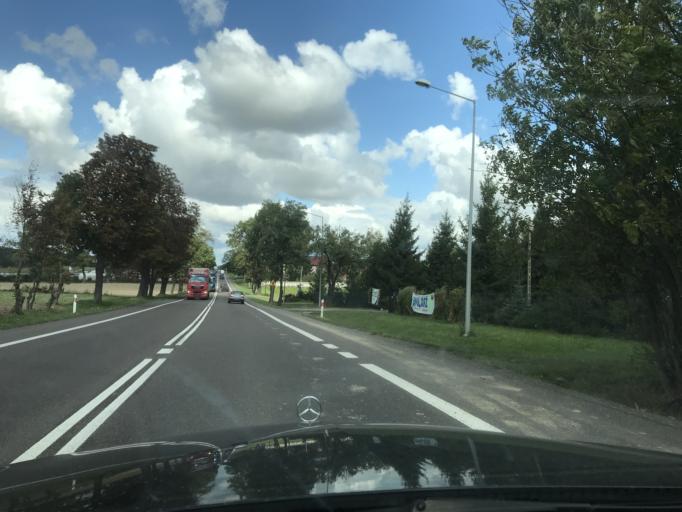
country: PL
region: Lublin Voivodeship
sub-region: Powiat lubelski
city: Niedrzwica Duza
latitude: 51.0596
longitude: 22.3835
